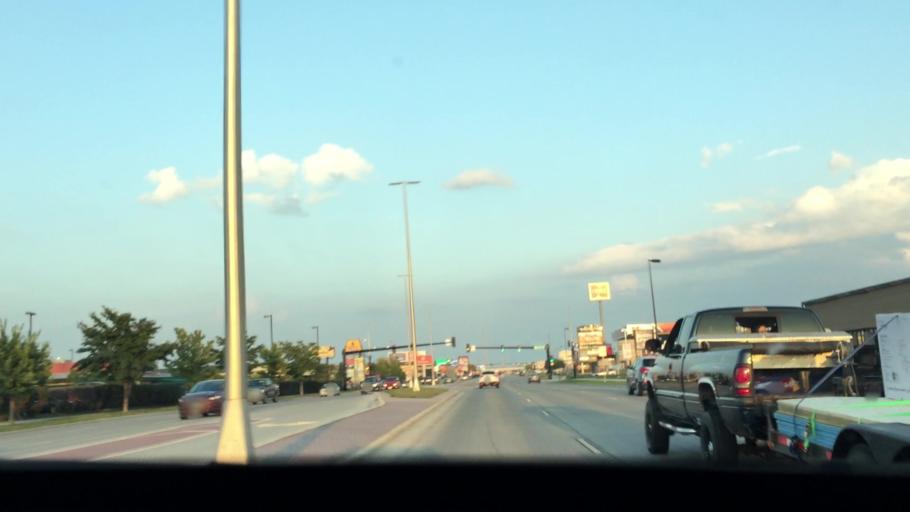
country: US
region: North Dakota
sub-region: Cass County
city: West Fargo
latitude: 46.8617
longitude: -96.8590
